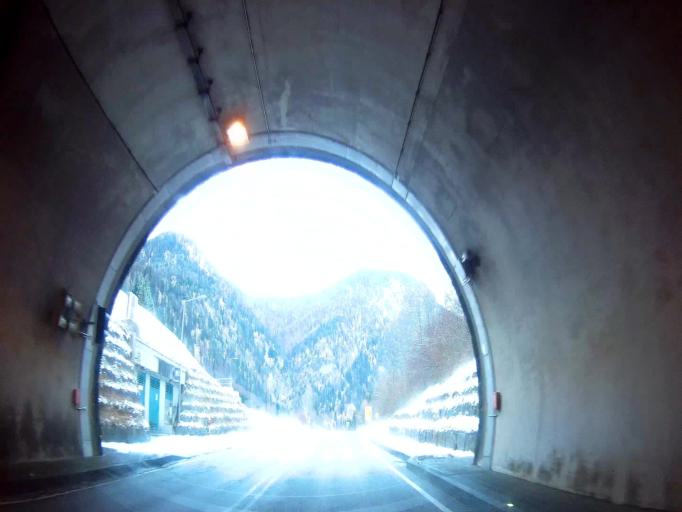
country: DE
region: Bavaria
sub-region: Upper Bavaria
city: Schneizlreuth
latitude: 47.6680
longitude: 12.7607
